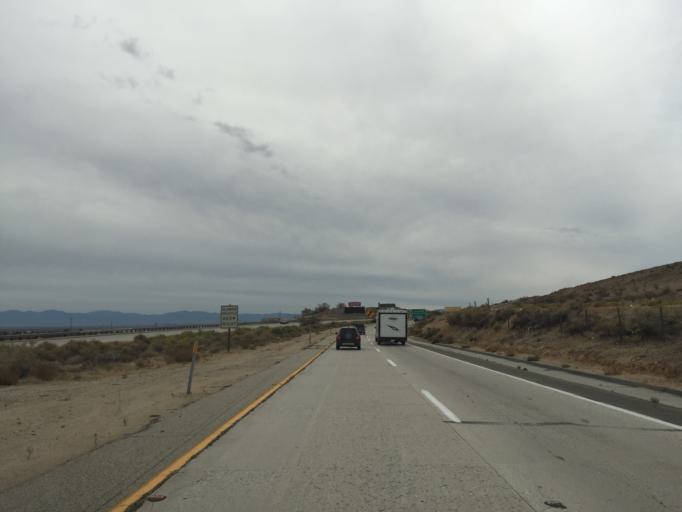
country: US
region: California
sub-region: Kern County
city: Rosamond
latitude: 34.8812
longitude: -118.1667
